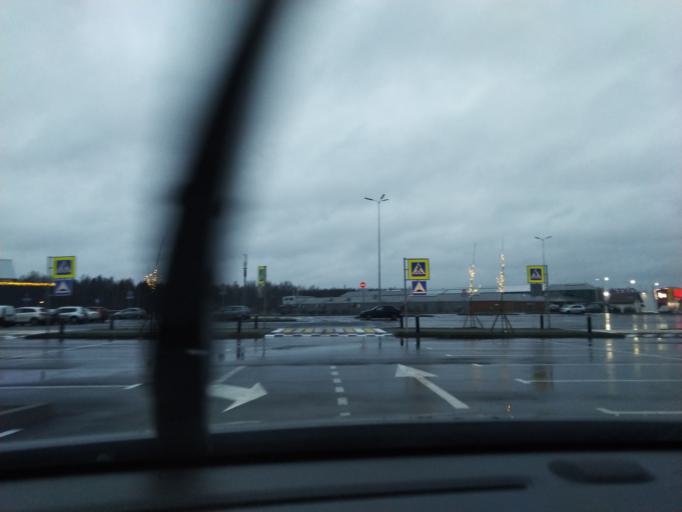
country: RU
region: St.-Petersburg
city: Gorelovo
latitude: 59.7930
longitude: 30.1459
